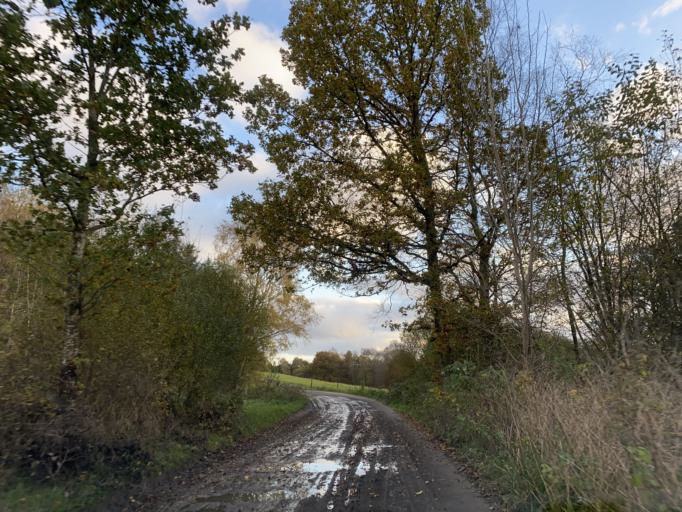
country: DK
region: Central Jutland
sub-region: Silkeborg Kommune
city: Svejbaek
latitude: 56.1795
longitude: 9.6049
